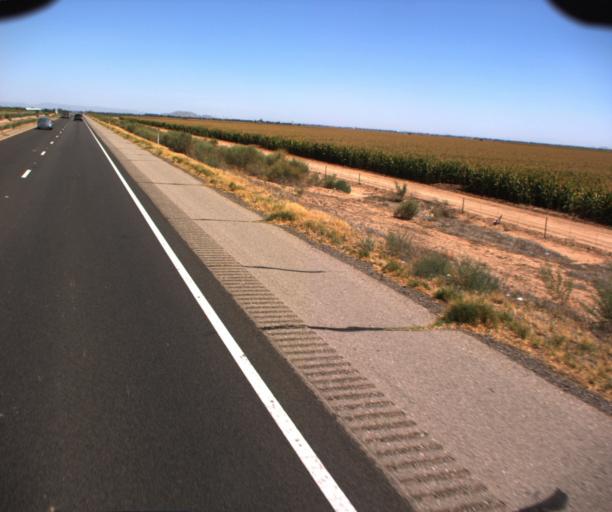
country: US
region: Arizona
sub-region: Pinal County
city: Maricopa
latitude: 33.0098
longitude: -112.0478
